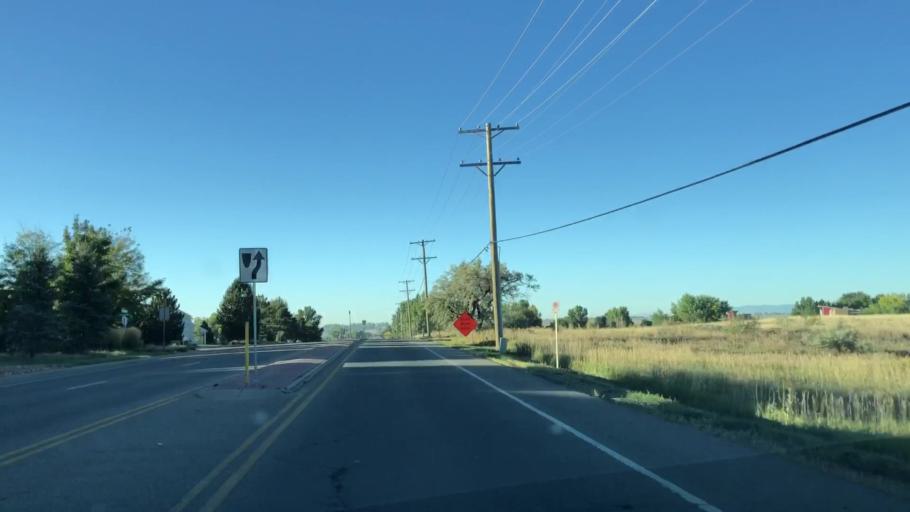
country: US
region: Colorado
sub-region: Larimer County
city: Loveland
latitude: 40.4124
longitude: -105.0210
